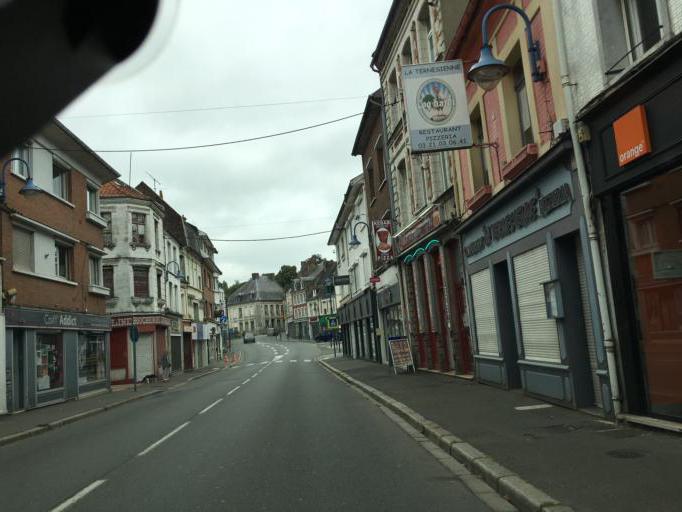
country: FR
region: Nord-Pas-de-Calais
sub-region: Departement du Pas-de-Calais
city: Saint-Pol-sur-Ternoise
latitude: 50.3818
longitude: 2.3363
